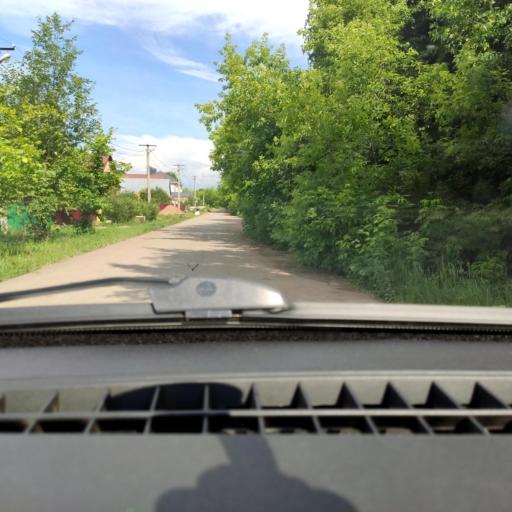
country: RU
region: Bashkortostan
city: Ufa
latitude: 54.7646
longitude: 55.9226
